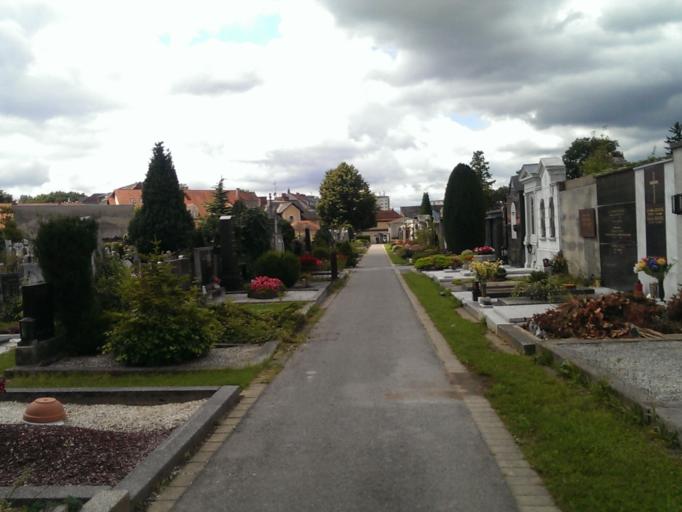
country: AT
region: Styria
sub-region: Graz Stadt
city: Graz
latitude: 47.0622
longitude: 15.4605
